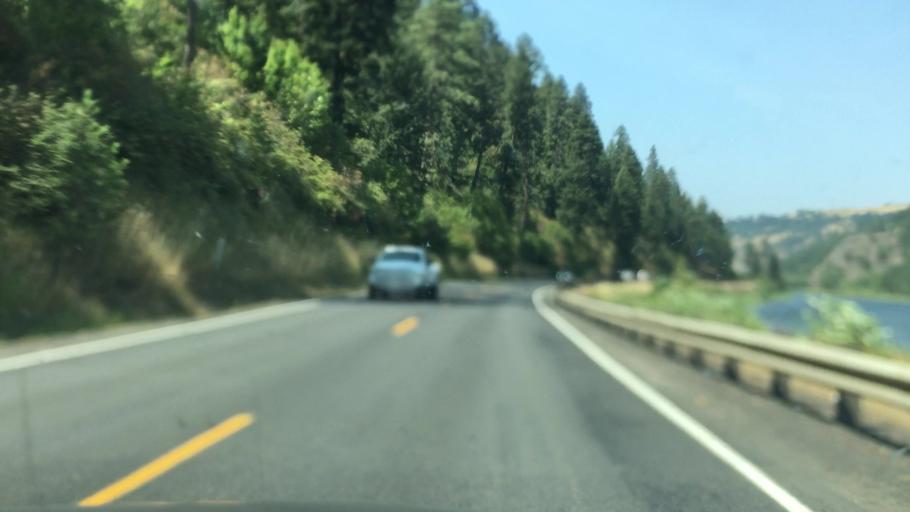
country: US
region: Idaho
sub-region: Clearwater County
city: Orofino
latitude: 46.4967
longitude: -116.4080
